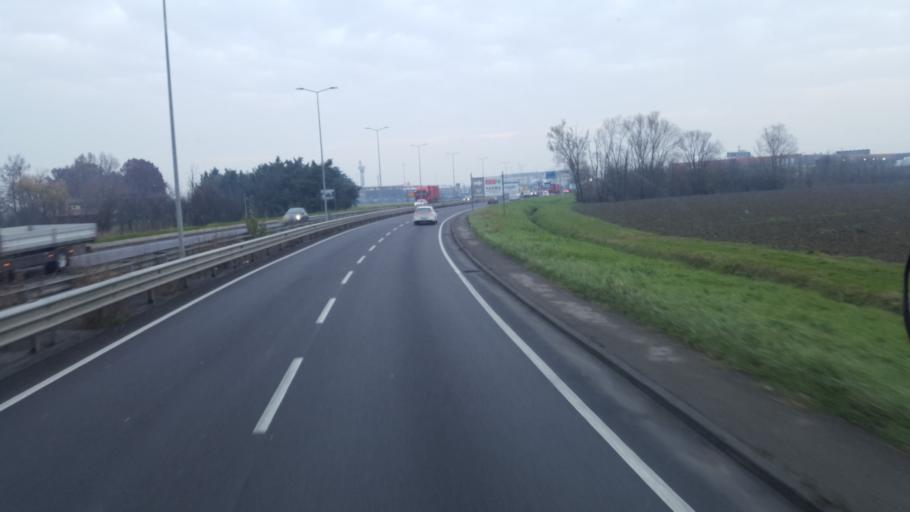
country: IT
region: Emilia-Romagna
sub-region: Provincia di Parma
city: Baganzola
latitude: 44.8330
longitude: 10.3317
